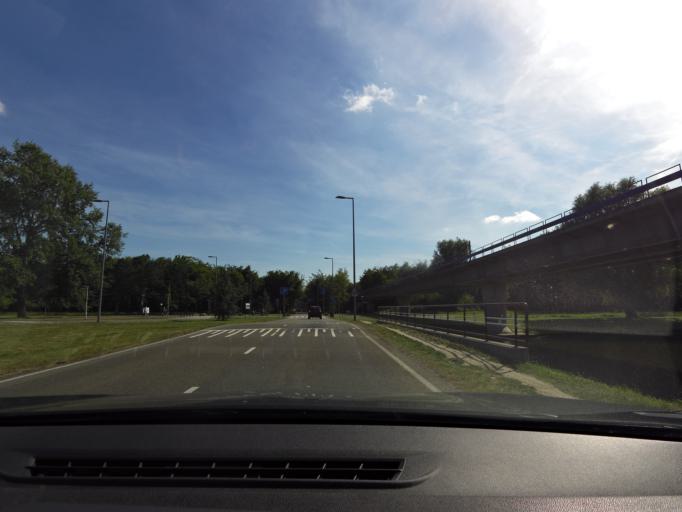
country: NL
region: South Holland
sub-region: Gemeente Rotterdam
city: Delfshaven
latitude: 51.8804
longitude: 4.4797
